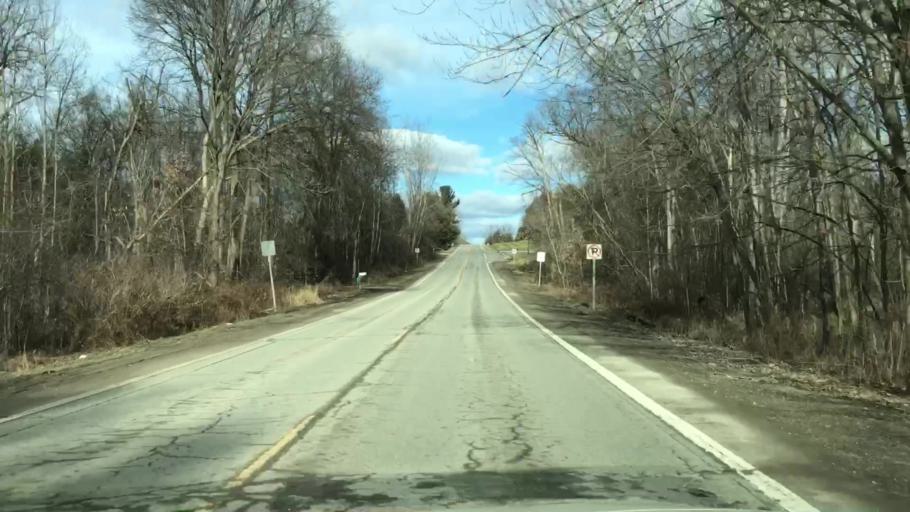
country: US
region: Michigan
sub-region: Oakland County
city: Lake Orion
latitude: 42.7552
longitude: -83.1974
